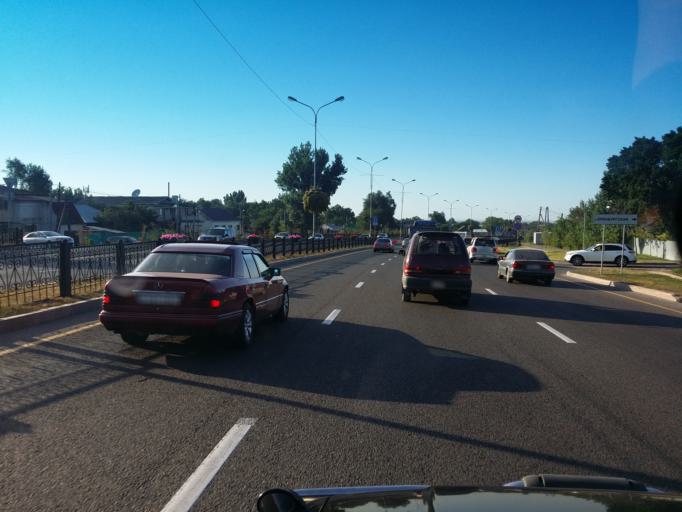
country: KZ
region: Almaty Qalasy
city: Almaty
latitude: 43.2728
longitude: 76.9849
